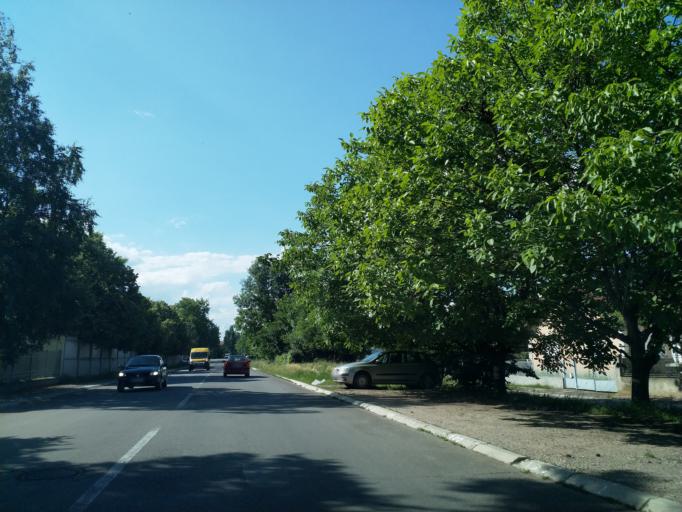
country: RS
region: Central Serbia
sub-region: Pomoravski Okrug
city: Paracin
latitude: 43.8542
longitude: 21.4083
